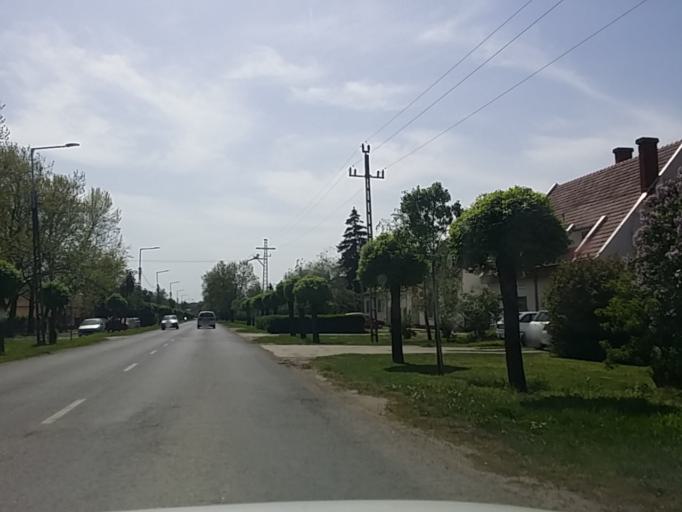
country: HU
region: Bekes
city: Gyula
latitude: 46.6530
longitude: 21.2834
